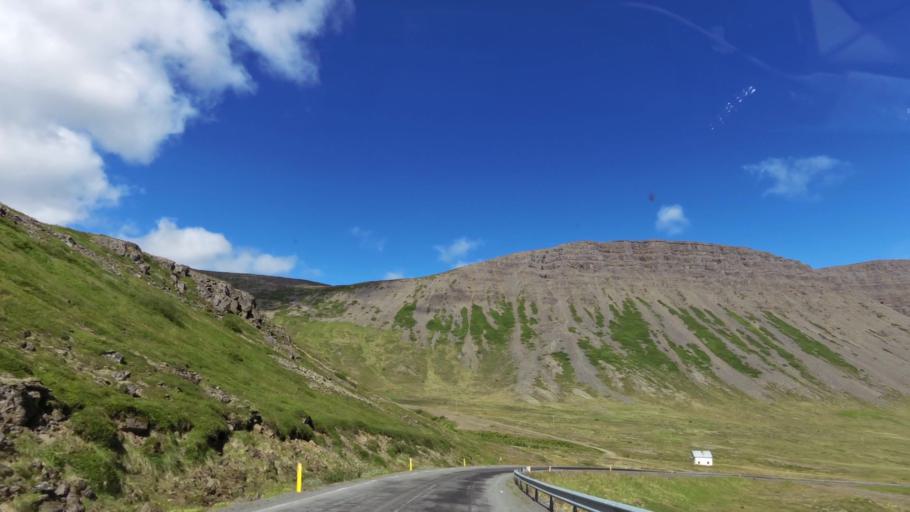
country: IS
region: Westfjords
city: Isafjoerdur
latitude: 65.6634
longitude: -23.6394
